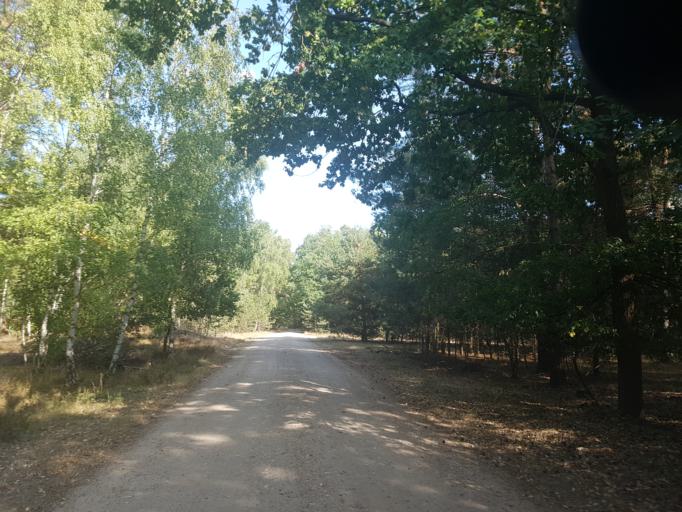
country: DE
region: Saxony-Anhalt
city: Jessen
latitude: 51.8690
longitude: 13.0084
